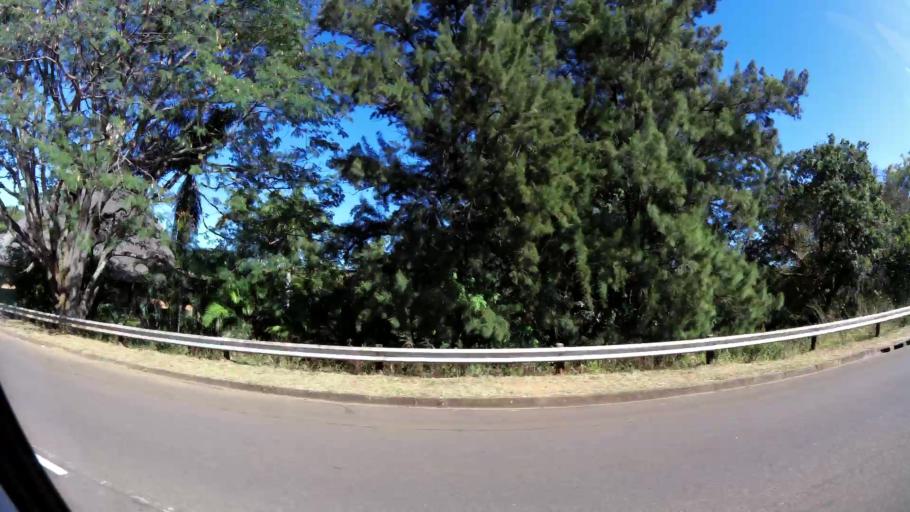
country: ZA
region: Limpopo
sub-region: Mopani District Municipality
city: Tzaneen
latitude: -23.8301
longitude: 30.1518
